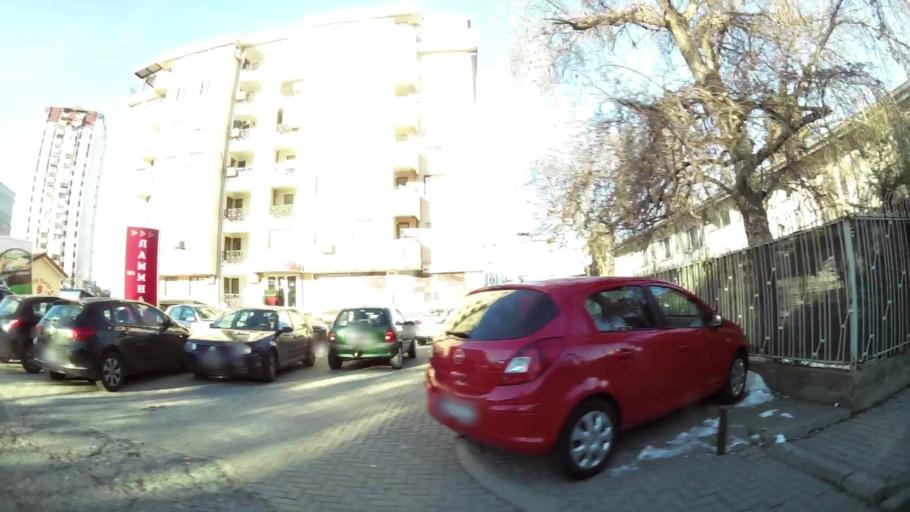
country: MK
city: Krushopek
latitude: 42.0065
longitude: 21.3832
